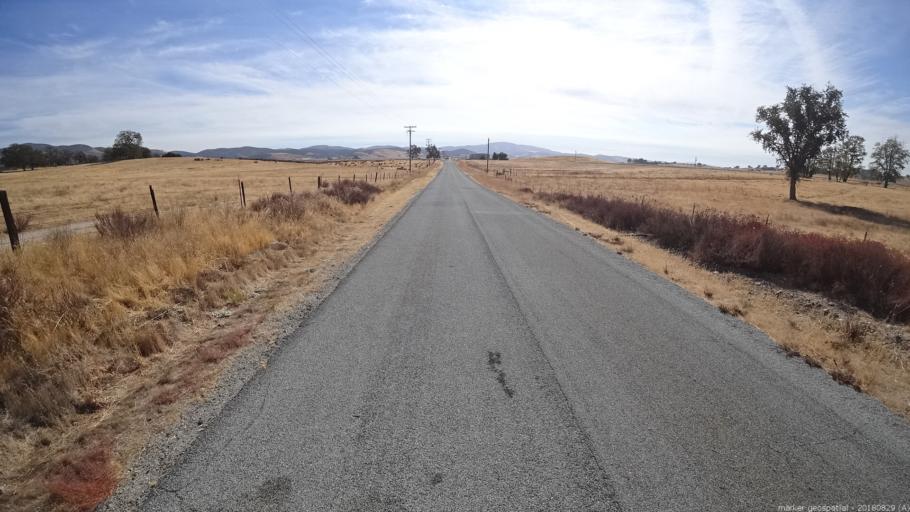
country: US
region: California
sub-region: Monterey County
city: King City
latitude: 35.9662
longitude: -121.1208
